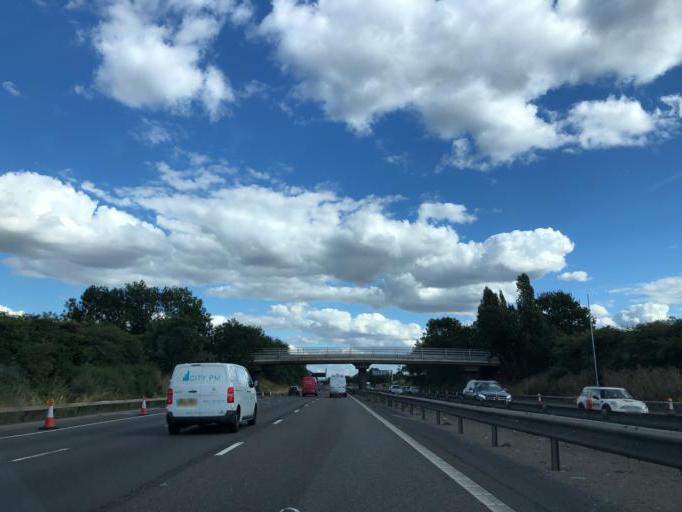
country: GB
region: England
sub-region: Milton Keynes
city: Gayhurst
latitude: 52.0900
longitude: -0.7553
